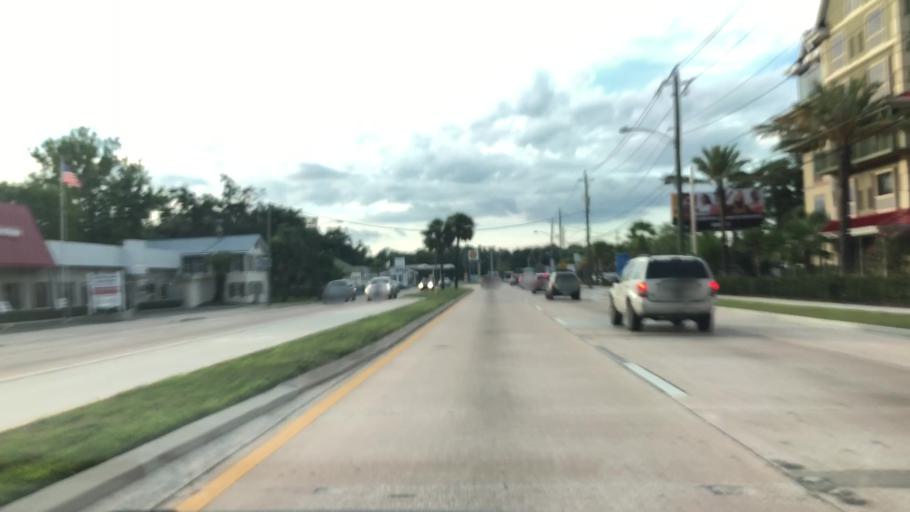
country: US
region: Florida
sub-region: Saint Johns County
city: Saint Augustine
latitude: 29.8885
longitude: -81.3232
